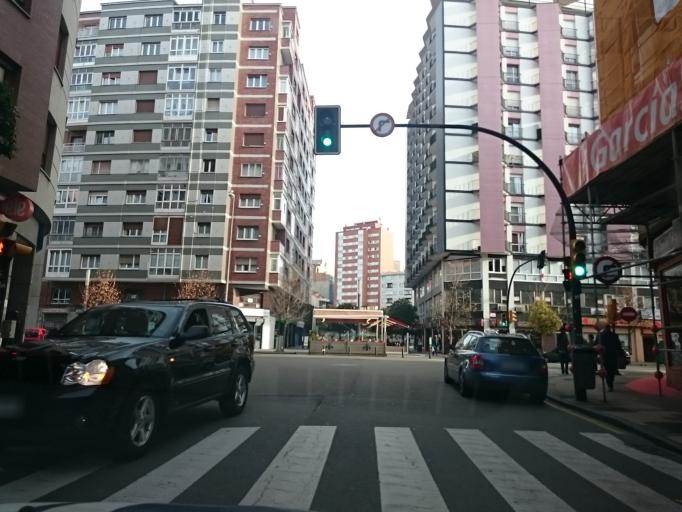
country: ES
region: Asturias
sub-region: Province of Asturias
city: Gijon
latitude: 43.5407
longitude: -5.6549
